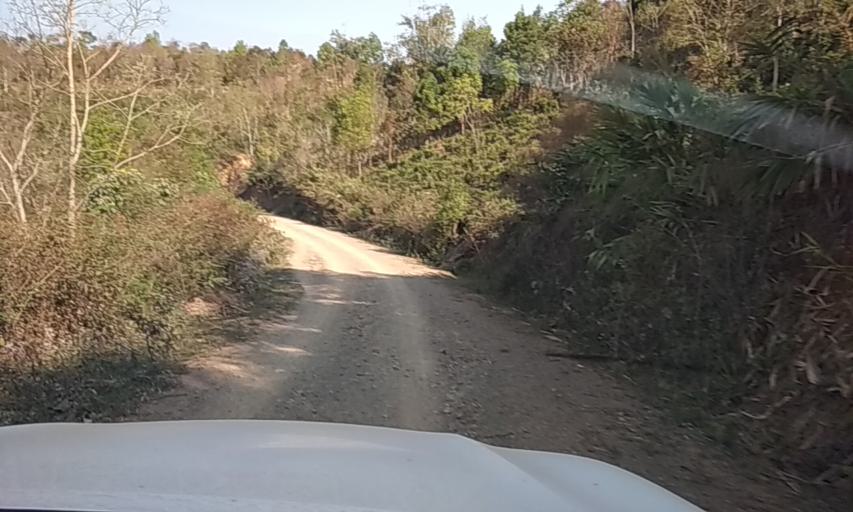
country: LA
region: Phongsali
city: Phongsali
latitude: 21.6933
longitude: 102.0938
